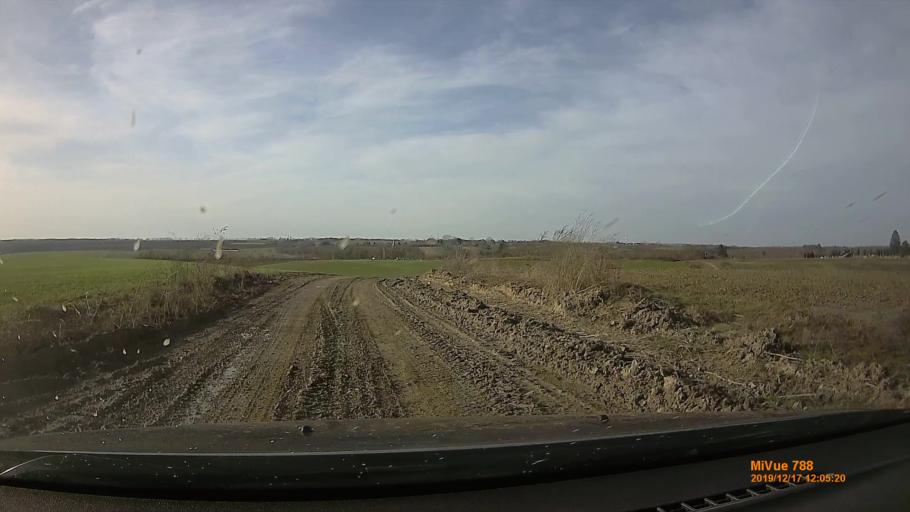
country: HU
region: Somogy
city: Kaposvar
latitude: 46.4581
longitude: 17.7810
